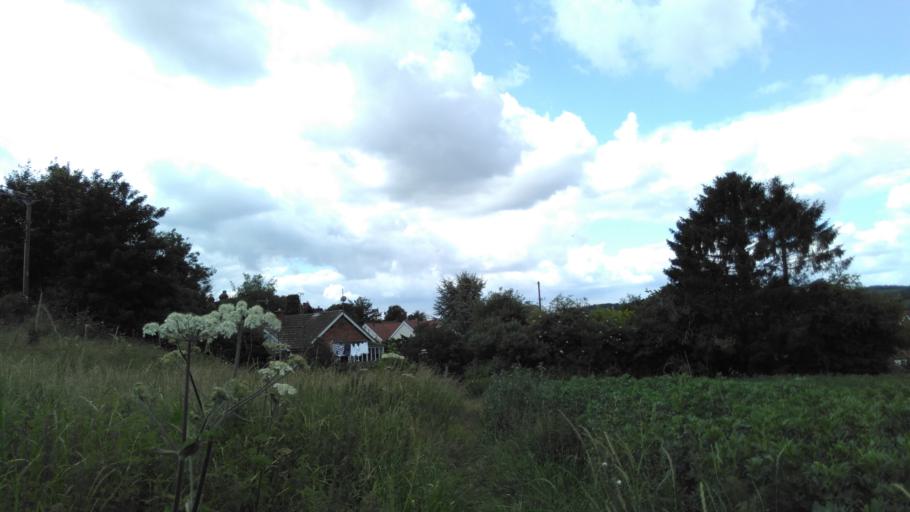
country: GB
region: England
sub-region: Kent
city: Chartham
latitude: 51.2534
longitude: 1.0099
